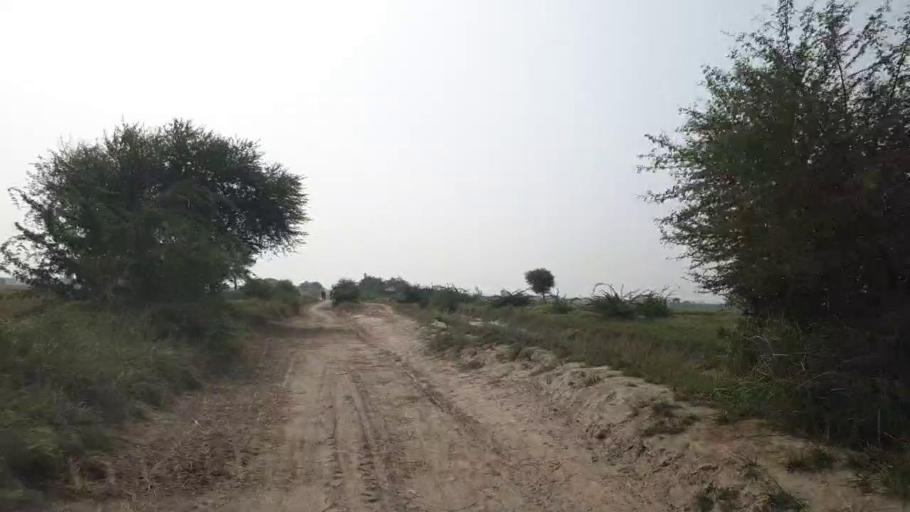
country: PK
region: Sindh
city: Kario
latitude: 24.7641
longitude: 68.5637
